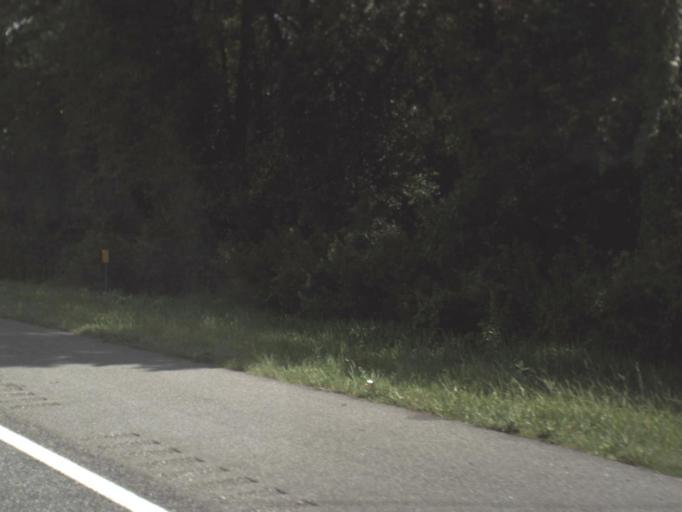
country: US
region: Florida
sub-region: Alachua County
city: High Springs
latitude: 29.9523
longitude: -82.5688
